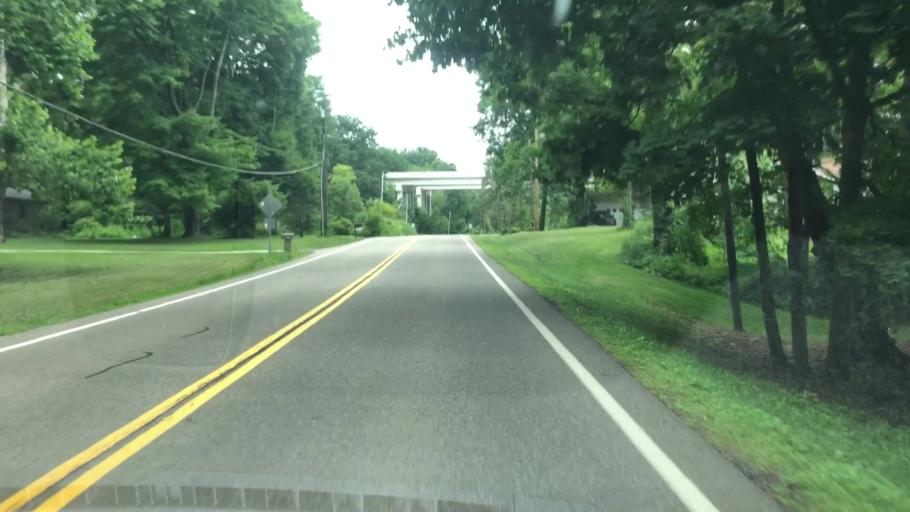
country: US
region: Ohio
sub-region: Summit County
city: Montrose-Ghent
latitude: 41.1572
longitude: -81.6293
